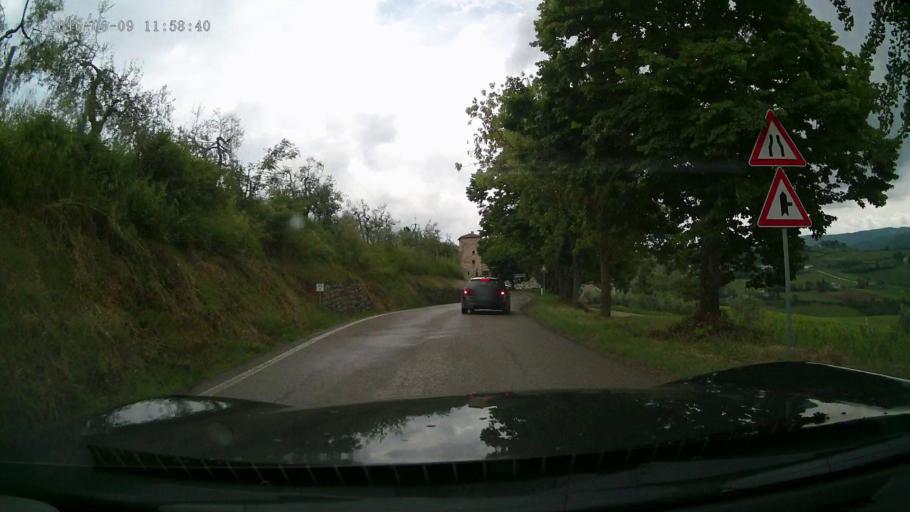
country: IT
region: Tuscany
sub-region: Province of Florence
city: Panzano in Chianti
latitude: 43.5463
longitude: 11.3081
